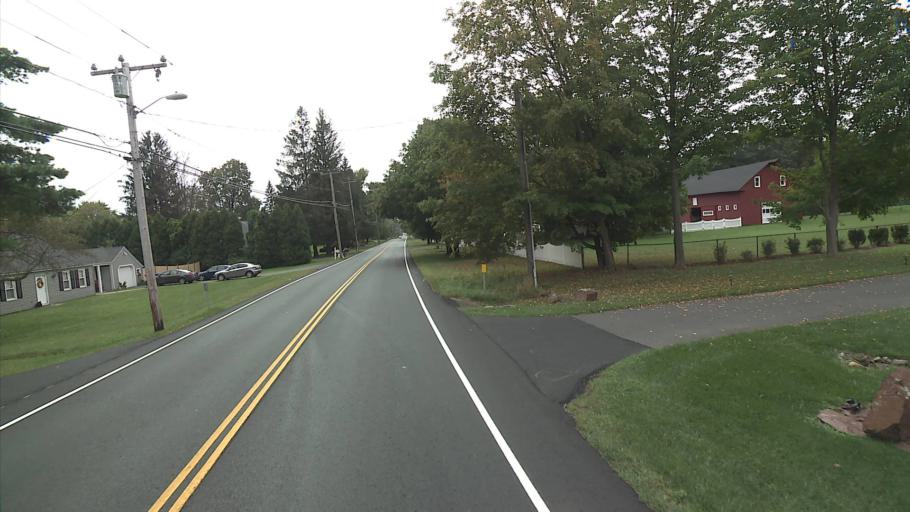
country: US
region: Connecticut
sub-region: Hartford County
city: Suffield Depot
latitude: 41.9999
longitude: -72.6965
